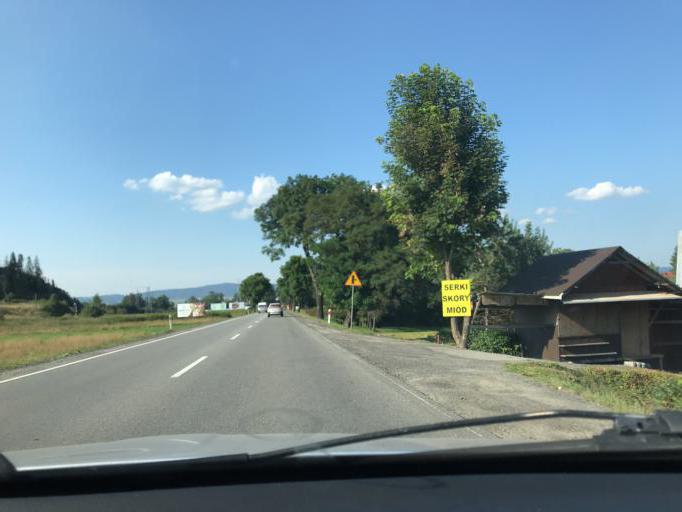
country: PL
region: Lesser Poland Voivodeship
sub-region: Powiat nowotarski
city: Szaflary
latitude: 49.4305
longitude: 20.0210
